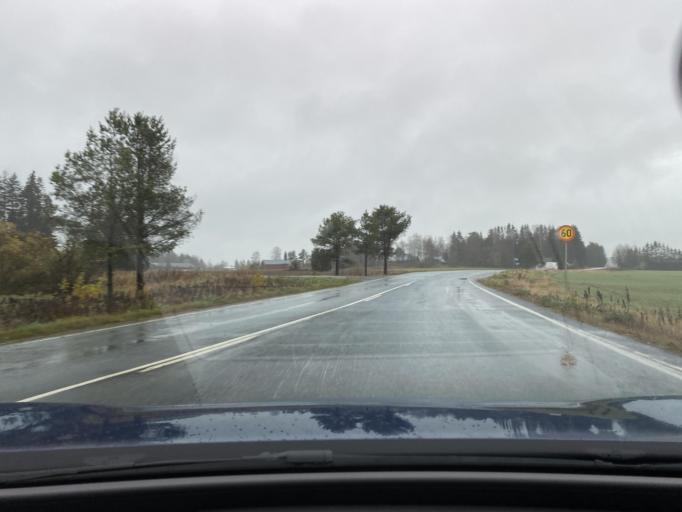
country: FI
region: Varsinais-Suomi
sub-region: Loimaa
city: Alastaro
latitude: 60.9342
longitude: 22.8652
